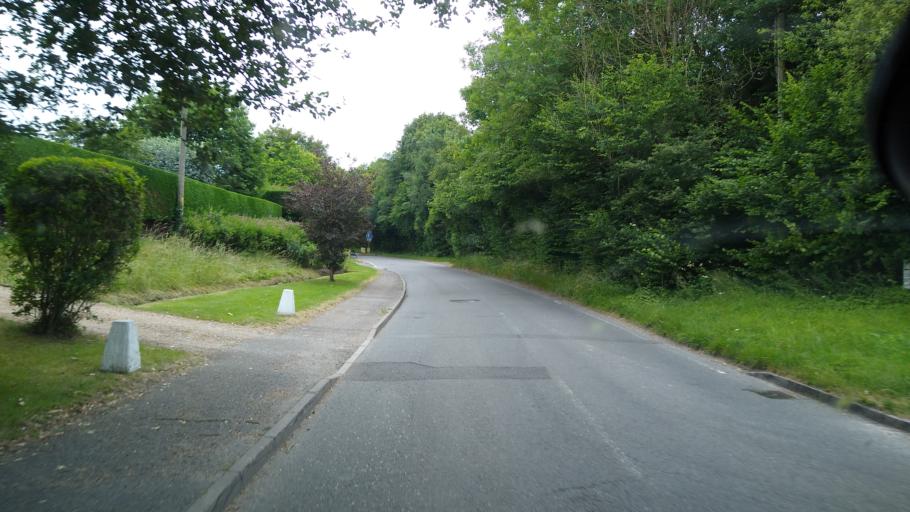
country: GB
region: England
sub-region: Hampshire
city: Alton
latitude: 51.0922
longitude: -0.9387
